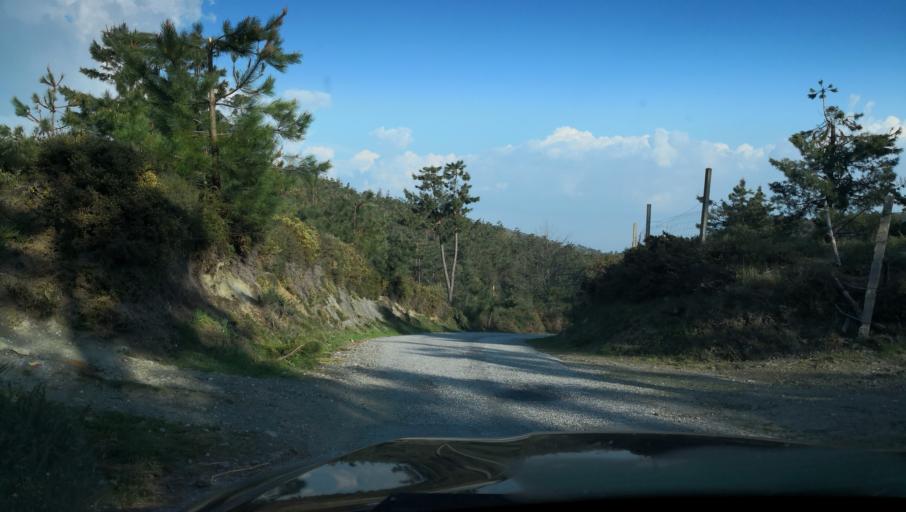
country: PT
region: Vila Real
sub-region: Vila Real
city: Vila Real
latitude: 41.3119
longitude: -7.8499
